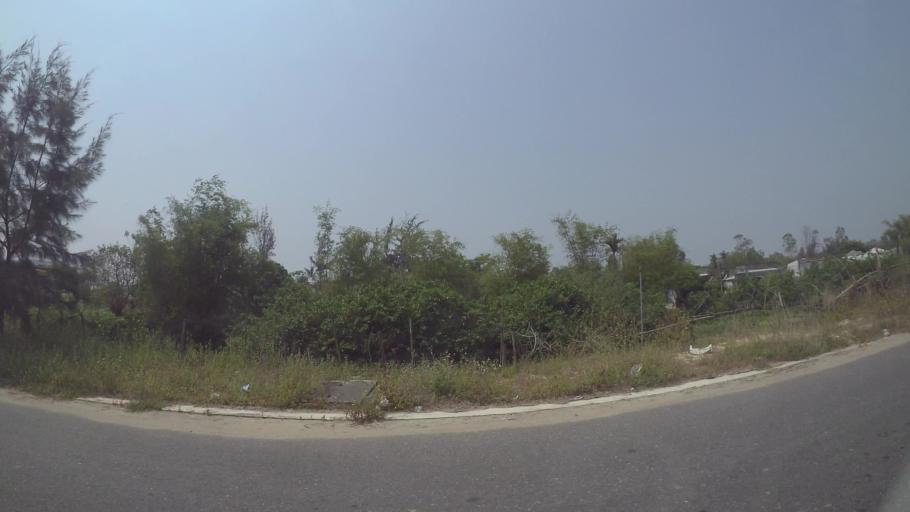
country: VN
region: Da Nang
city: Ngu Hanh Son
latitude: 15.9816
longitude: 108.2615
